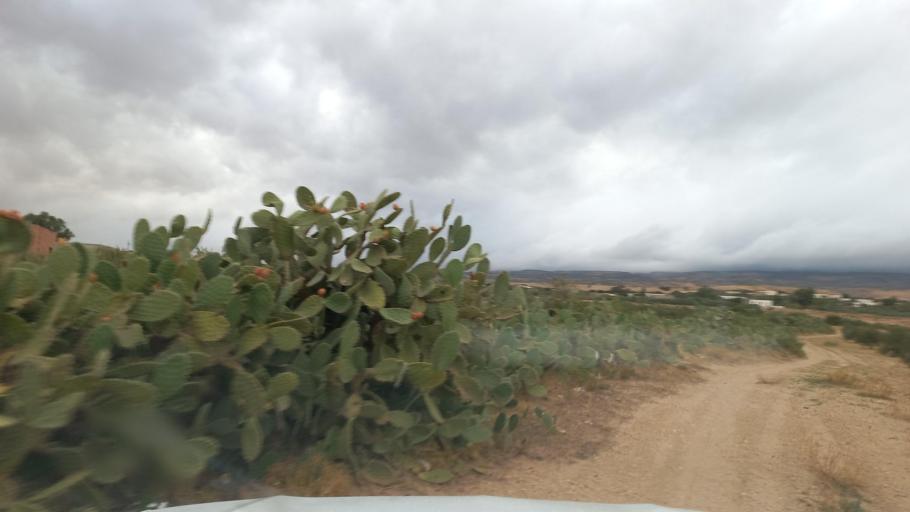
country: TN
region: Al Qasrayn
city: Kasserine
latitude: 35.2759
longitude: 8.9477
